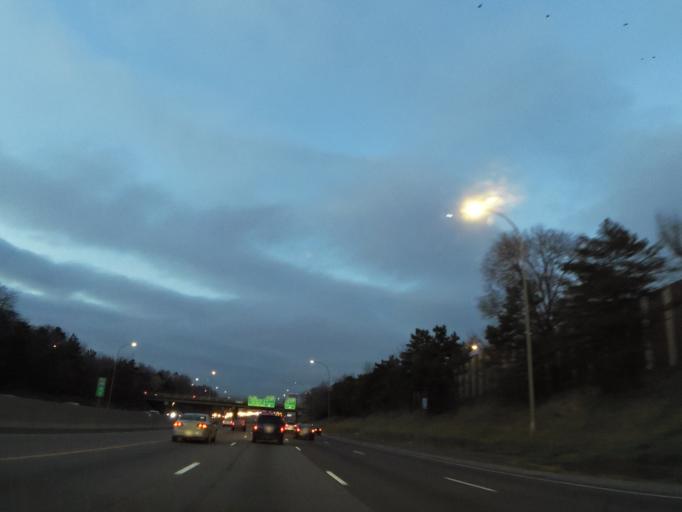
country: US
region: Minnesota
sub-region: Hennepin County
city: Minneapolis
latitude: 44.9379
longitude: -93.2746
